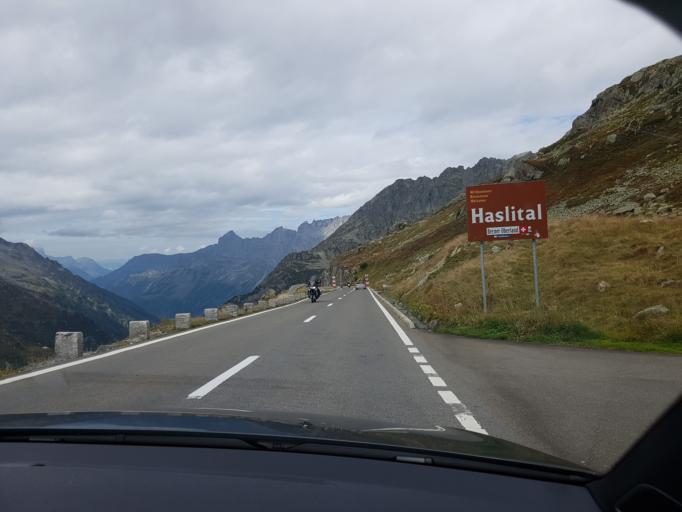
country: CH
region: Obwalden
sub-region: Obwalden
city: Engelberg
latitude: 46.7294
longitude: 8.4443
